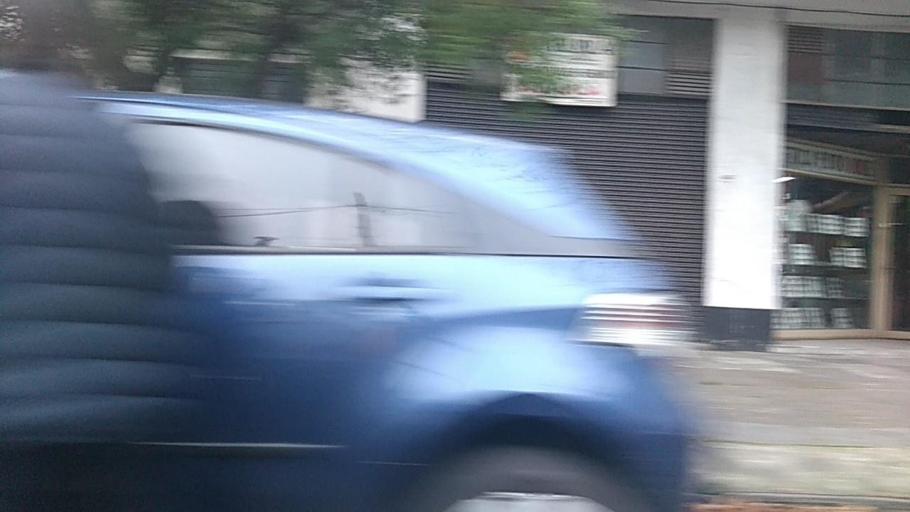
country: AR
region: Buenos Aires F.D.
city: Villa Santa Rita
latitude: -34.6058
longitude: -58.5075
